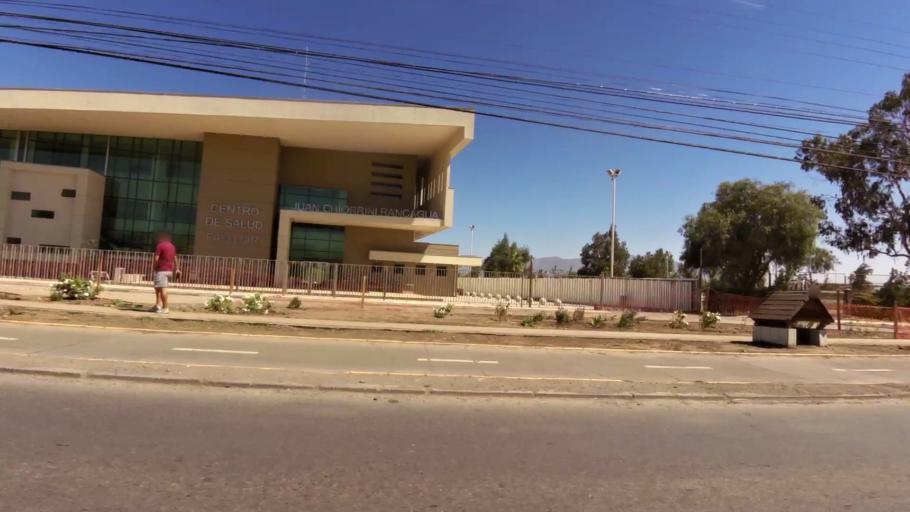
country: CL
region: O'Higgins
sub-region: Provincia de Cachapoal
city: Rancagua
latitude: -34.1639
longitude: -70.7137
